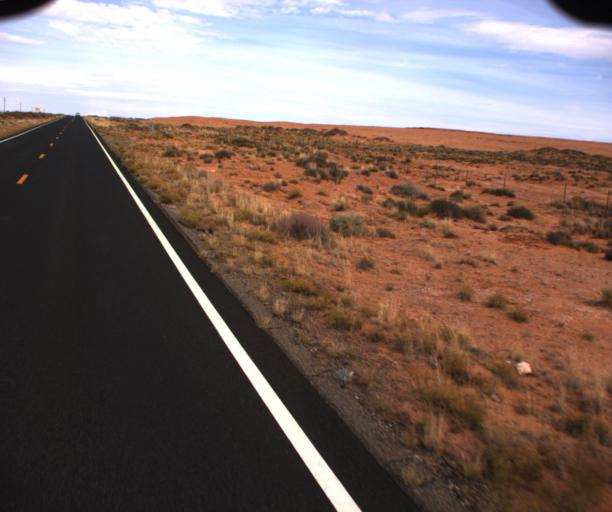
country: US
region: Arizona
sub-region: Apache County
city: Many Farms
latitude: 36.8213
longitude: -109.6452
